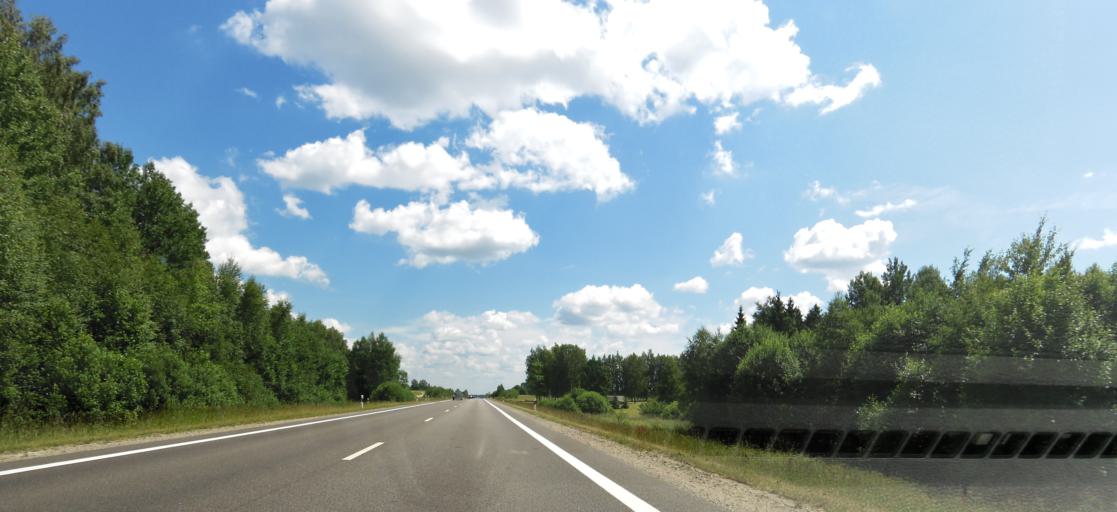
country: LT
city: Skaidiskes
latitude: 54.5707
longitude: 25.6231
